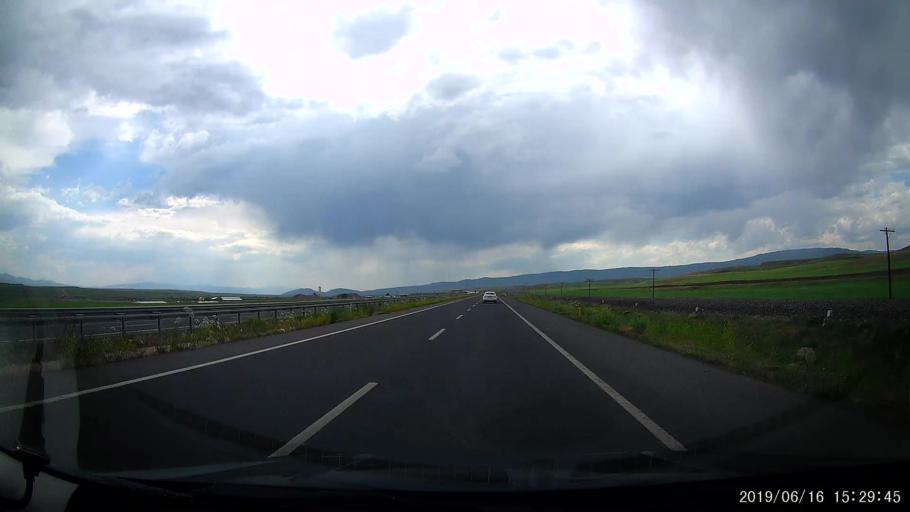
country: TR
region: Erzurum
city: Horasan
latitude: 40.0324
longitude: 42.1244
